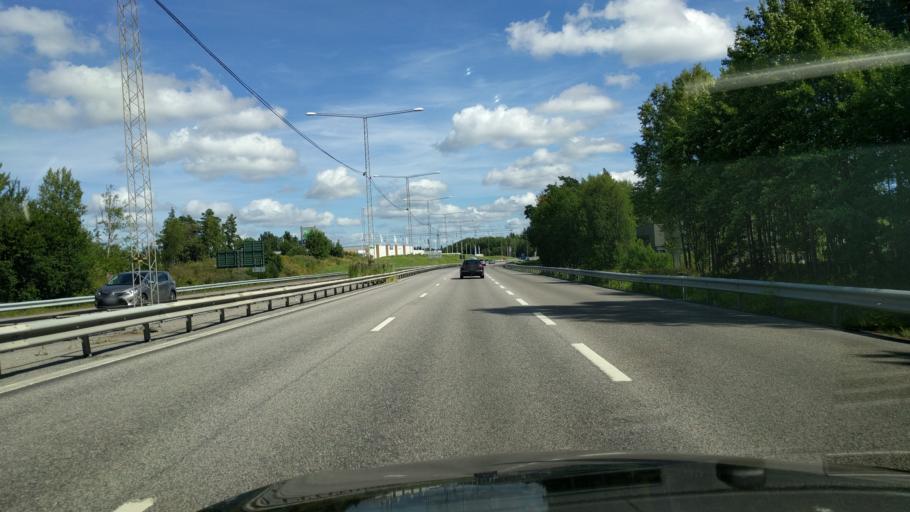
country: SE
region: Stockholm
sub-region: Danderyds Kommun
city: Djursholm
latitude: 59.4189
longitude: 18.0425
